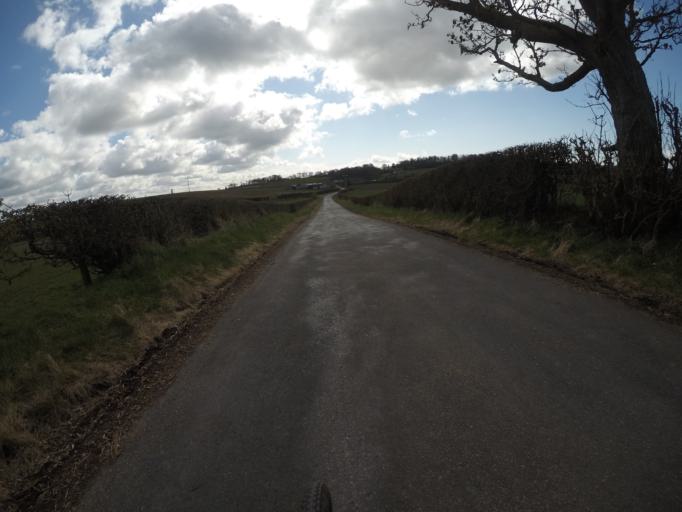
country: GB
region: Scotland
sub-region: South Ayrshire
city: Dundonald
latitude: 55.5897
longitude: -4.5785
